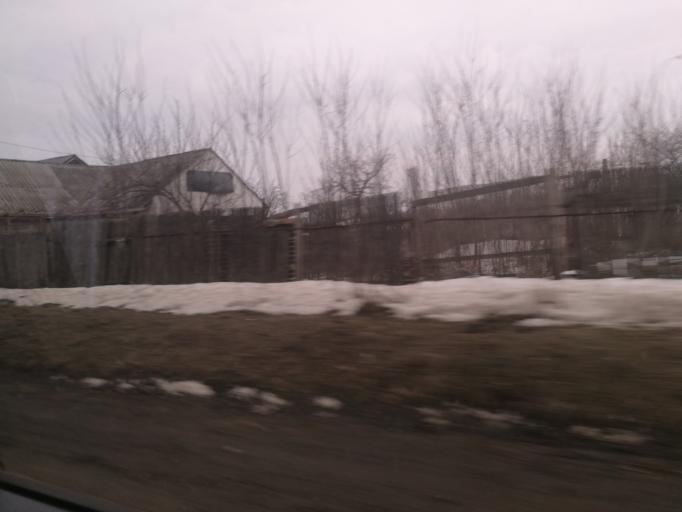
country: RO
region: Iasi
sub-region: Comuna Ruginoasa
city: Ruginoasa
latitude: 47.2459
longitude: 26.8539
